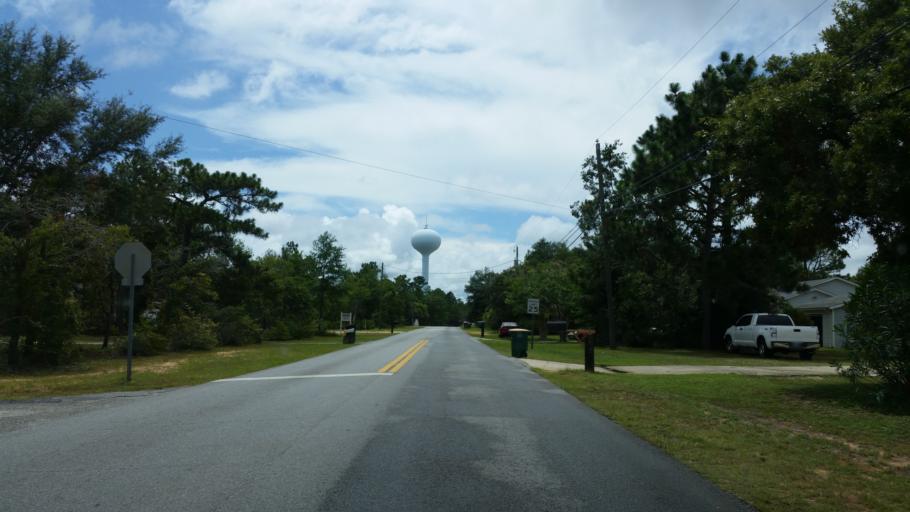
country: US
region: Florida
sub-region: Santa Rosa County
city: Navarre
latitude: 30.4323
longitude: -86.8592
